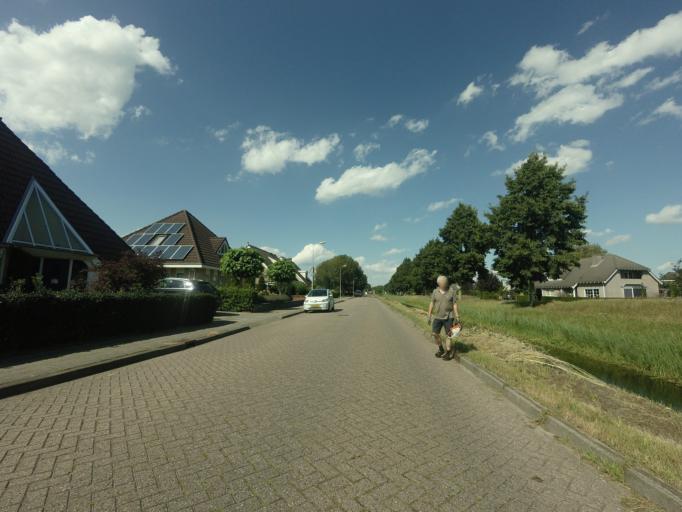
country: NL
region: Drenthe
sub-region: Gemeente Hoogeveen
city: Hoogeveen
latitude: 52.5932
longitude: 6.4606
